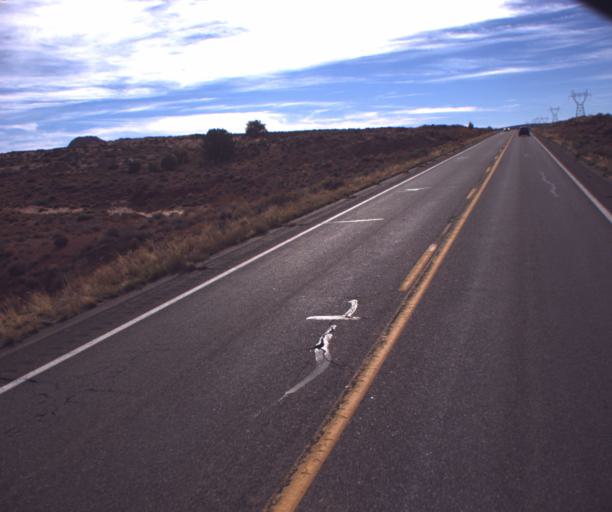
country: US
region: Arizona
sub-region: Coconino County
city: LeChee
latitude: 36.8505
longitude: -111.3332
